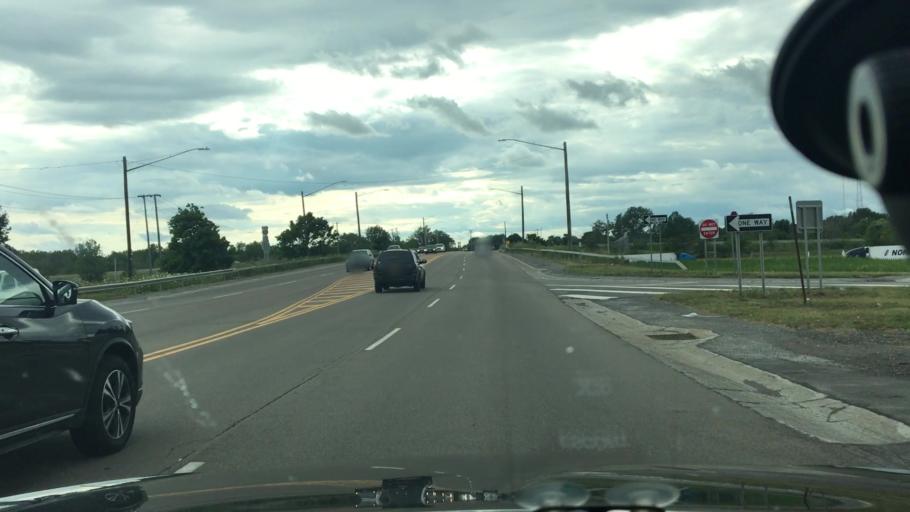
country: US
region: New York
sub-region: Erie County
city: West Seneca
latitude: 42.8285
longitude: -78.7887
